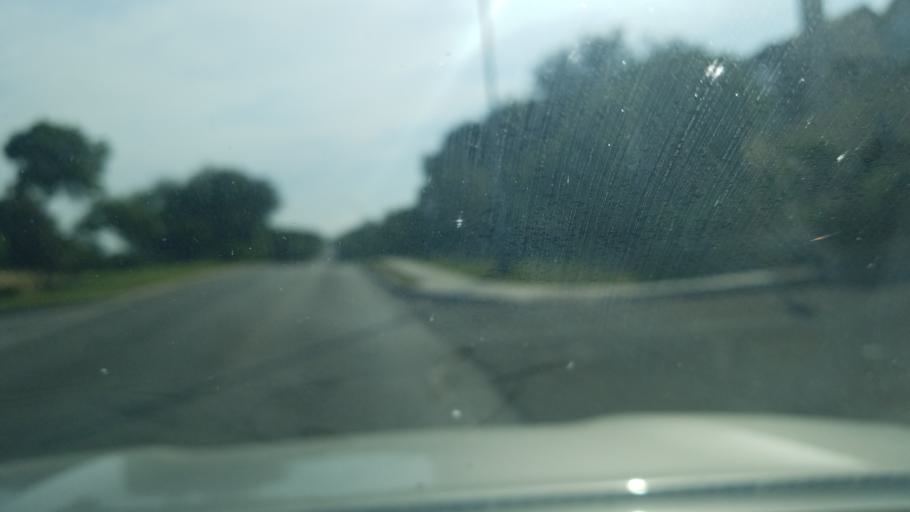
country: US
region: Texas
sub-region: Bexar County
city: Hollywood Park
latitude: 29.6263
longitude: -98.5012
